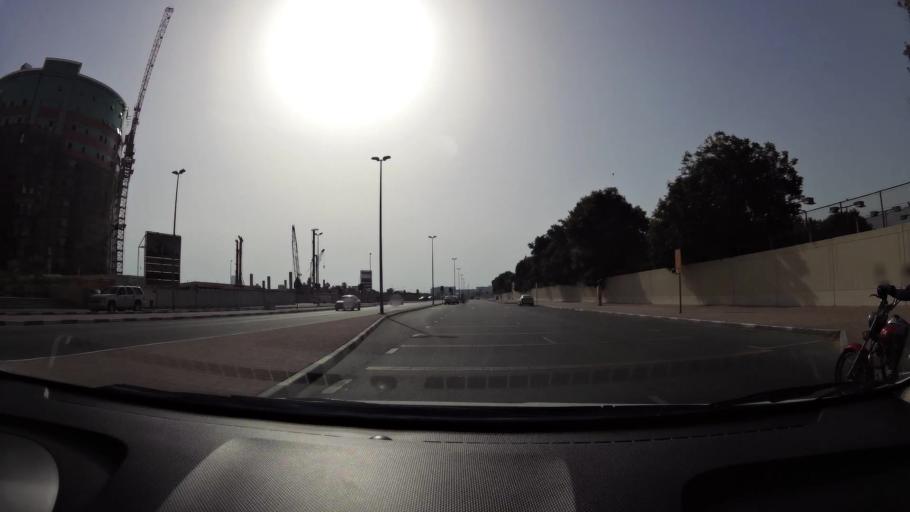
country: AE
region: Ash Shariqah
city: Sharjah
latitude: 25.2353
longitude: 55.3550
